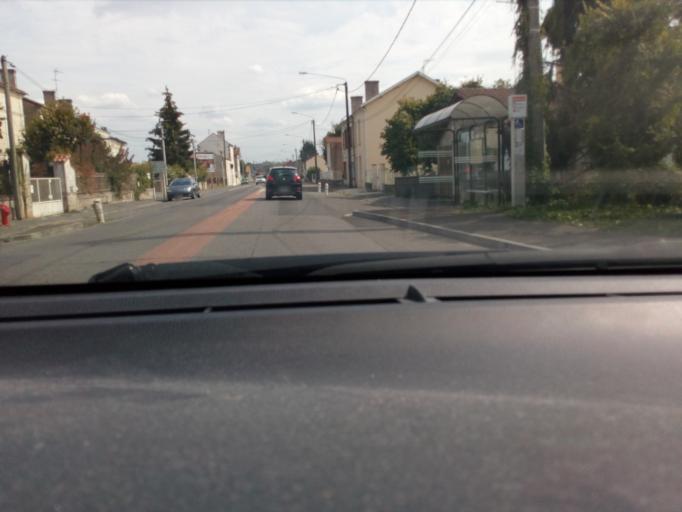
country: FR
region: Poitou-Charentes
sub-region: Departement de la Charente
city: Saint-Yrieix-sur-Charente
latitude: 45.6697
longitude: 0.1172
